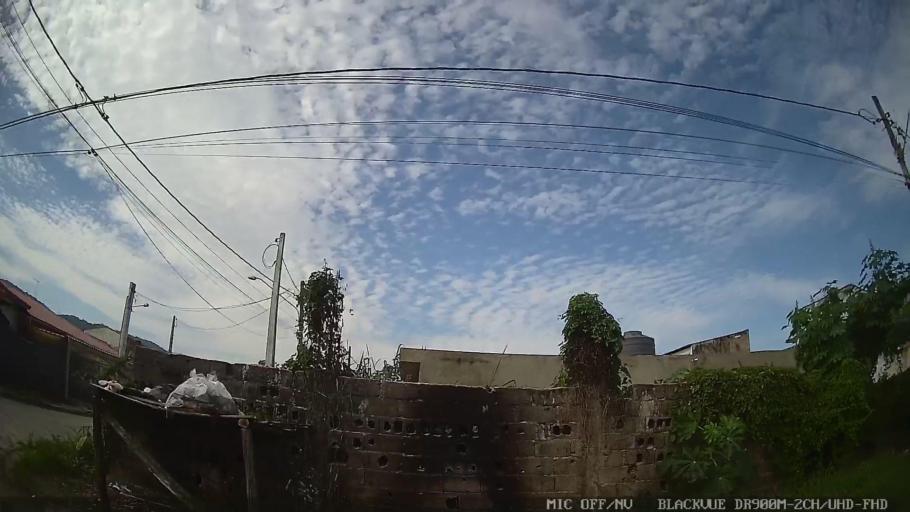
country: BR
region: Sao Paulo
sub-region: Itanhaem
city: Itanhaem
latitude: -24.1570
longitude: -46.7529
